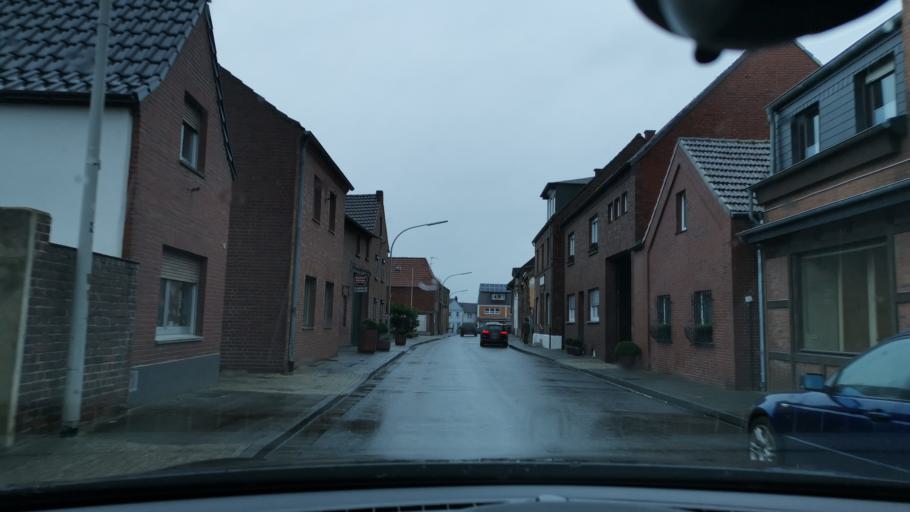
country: DE
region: North Rhine-Westphalia
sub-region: Regierungsbezirk Dusseldorf
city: Grevenbroich
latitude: 51.0645
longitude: 6.5625
